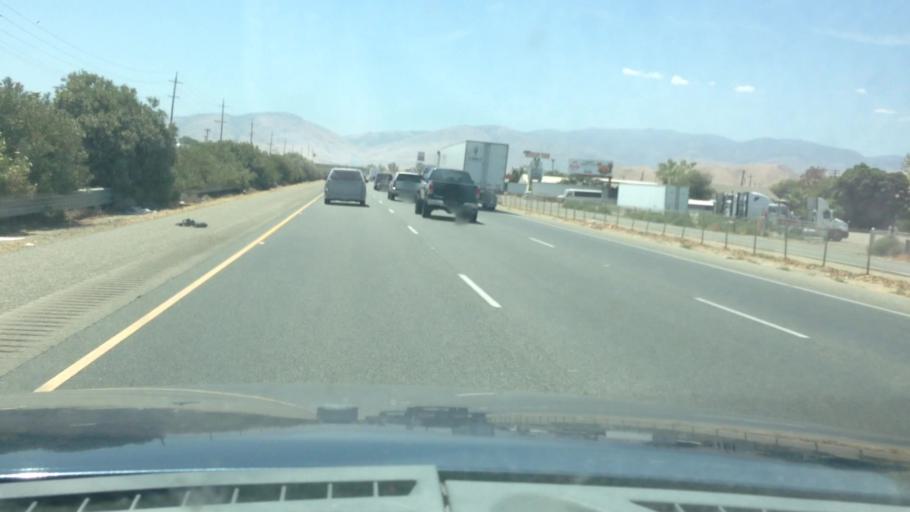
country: US
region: California
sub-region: Kern County
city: Weedpatch
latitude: 35.0658
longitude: -118.9704
